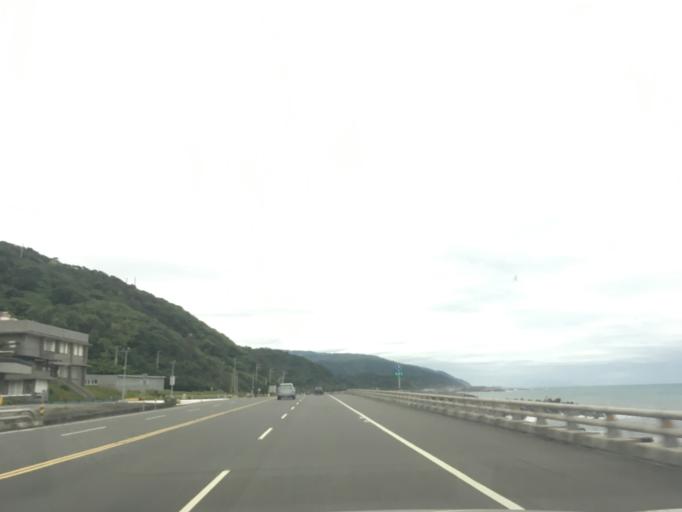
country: TW
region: Taiwan
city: Hengchun
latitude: 22.3229
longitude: 120.8919
